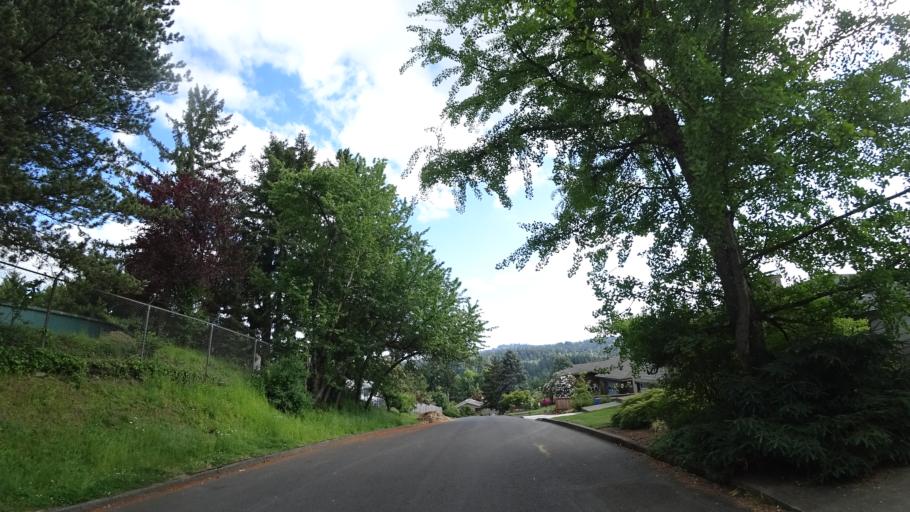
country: US
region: Oregon
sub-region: Washington County
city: Garden Home-Whitford
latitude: 45.4793
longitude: -122.7175
